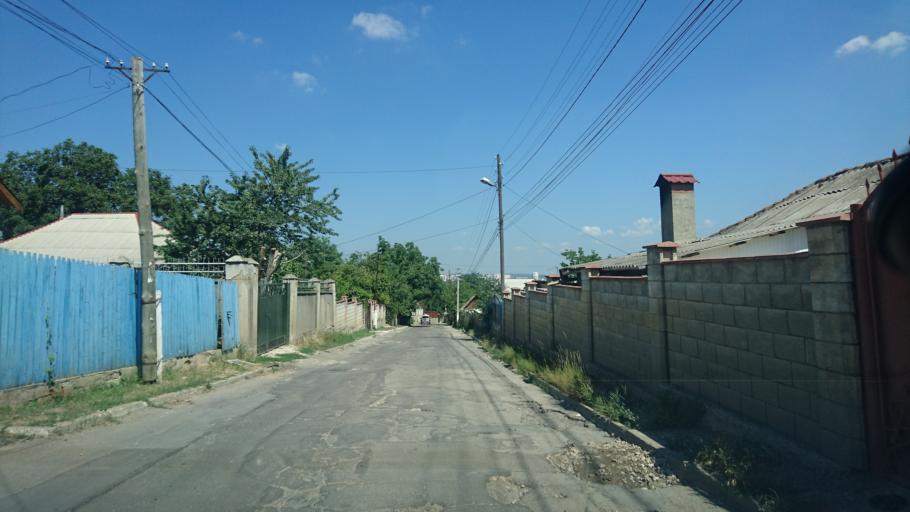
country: MD
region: Laloveni
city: Ialoveni
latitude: 47.0075
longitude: 28.7668
